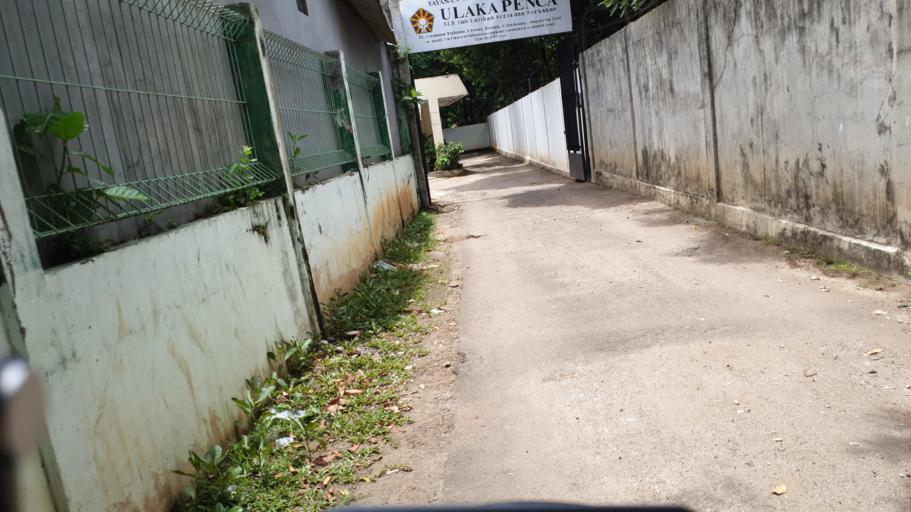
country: ID
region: West Java
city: Pamulang
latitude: -6.3048
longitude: 106.7837
